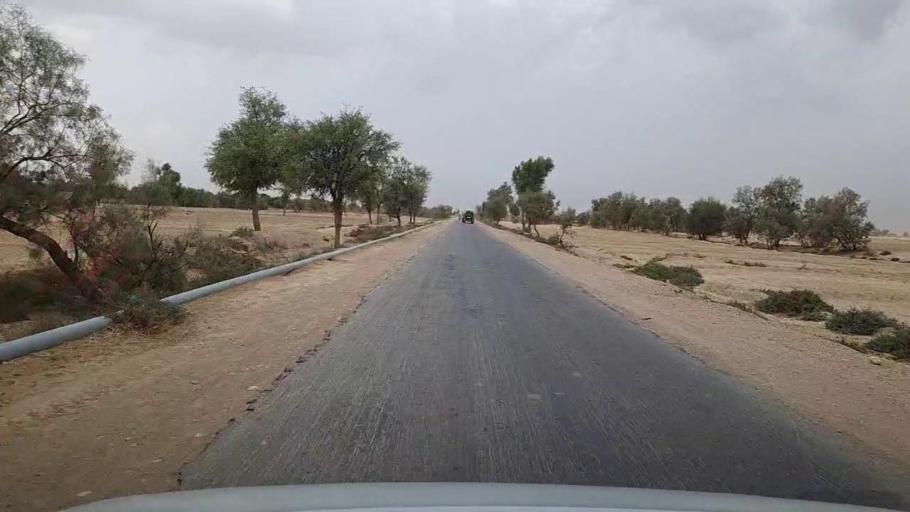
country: PK
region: Sindh
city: Sehwan
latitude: 26.3275
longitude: 67.7254
